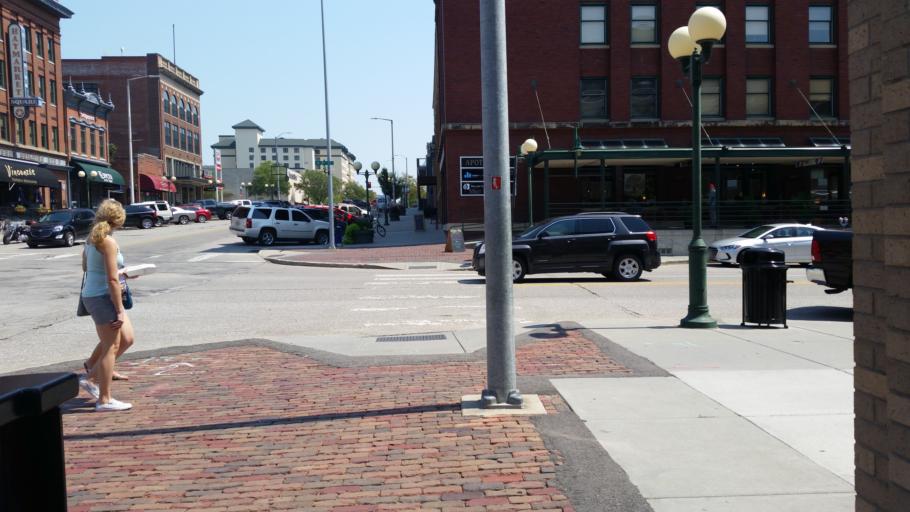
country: US
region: Nebraska
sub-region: Lancaster County
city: Lincoln
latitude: 40.8148
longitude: -96.7102
